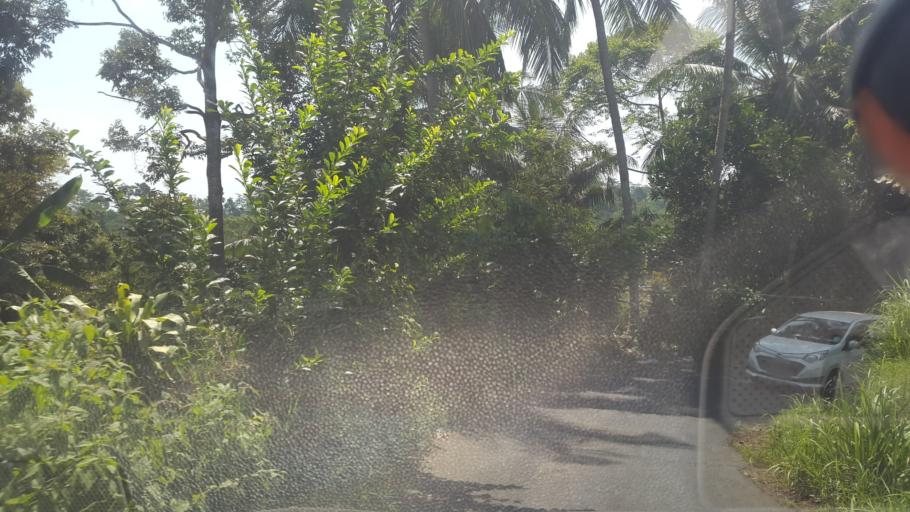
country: ID
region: West Java
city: Cicurug
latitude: -6.8856
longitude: 106.8089
